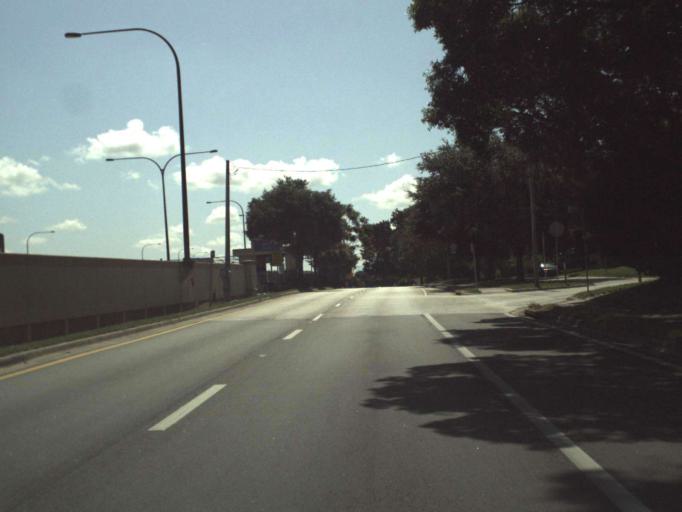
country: US
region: Florida
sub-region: Orange County
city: Orlando
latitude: 28.5378
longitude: -81.3559
